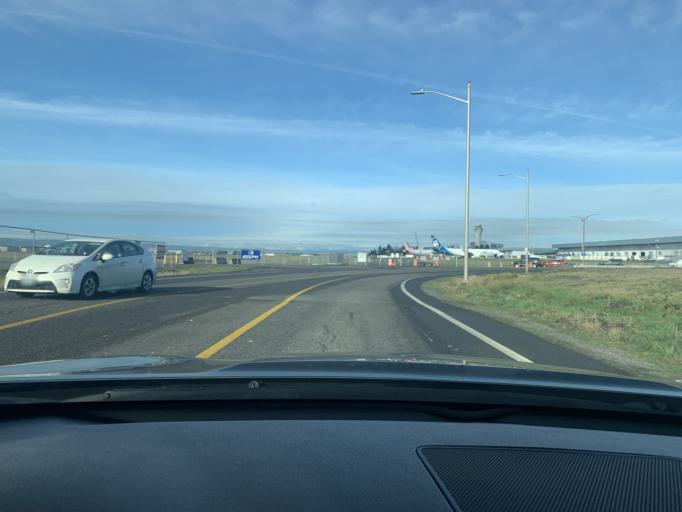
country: US
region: Washington
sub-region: Clark County
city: Orchards
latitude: 45.5802
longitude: -122.5769
